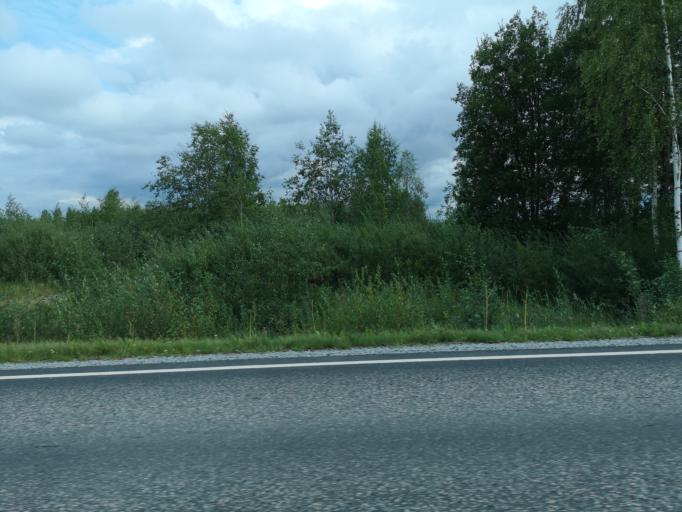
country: FI
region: Central Finland
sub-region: Jyvaeskylae
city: Hankasalmi
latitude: 62.3661
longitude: 26.4482
